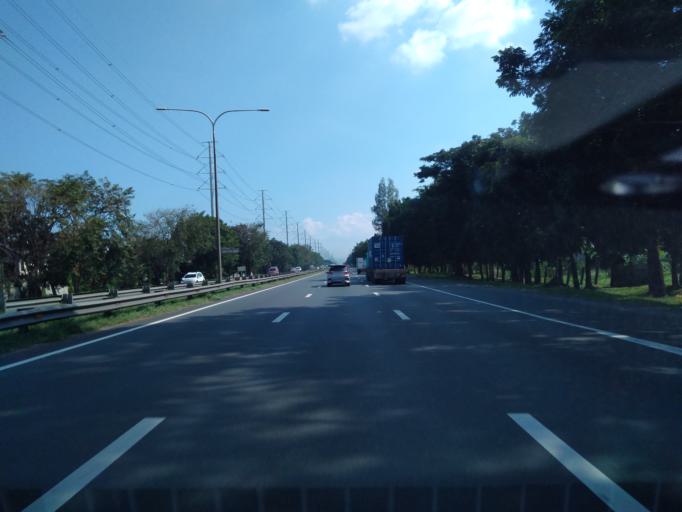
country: PH
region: Calabarzon
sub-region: Province of Laguna
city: Pulong Santa Cruz
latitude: 14.2829
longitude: 121.0896
